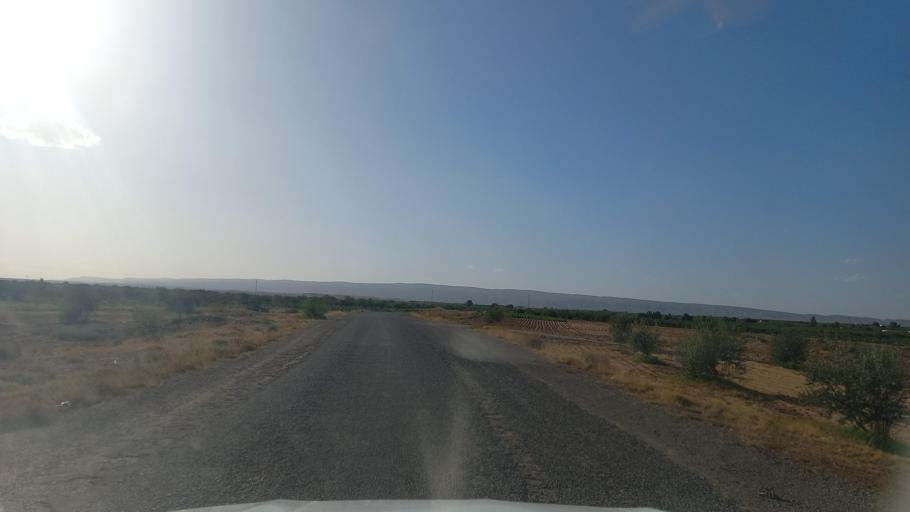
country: TN
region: Al Qasrayn
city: Kasserine
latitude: 35.2594
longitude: 9.0321
